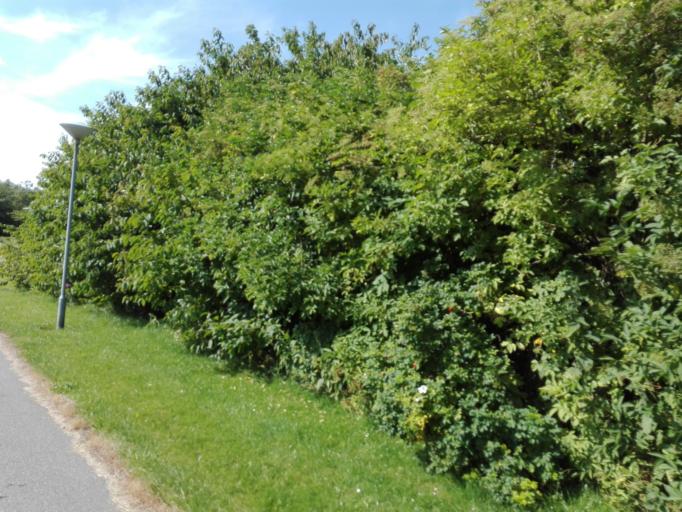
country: DK
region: Central Jutland
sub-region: Arhus Kommune
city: Tranbjerg
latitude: 56.0960
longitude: 10.1173
